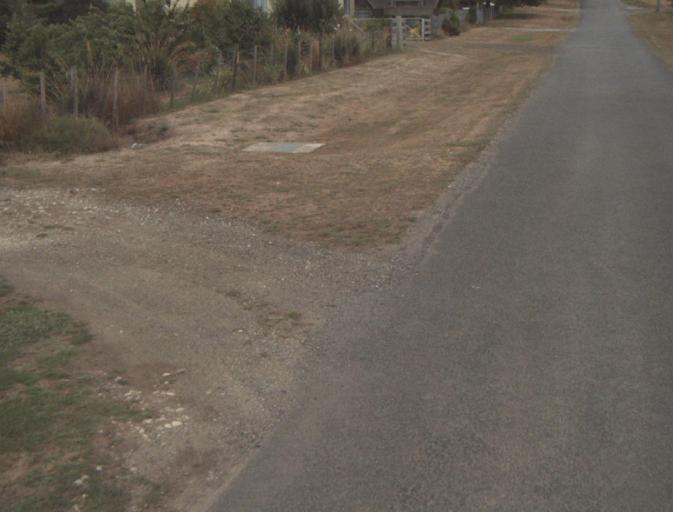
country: AU
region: Tasmania
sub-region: Launceston
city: Mayfield
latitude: -41.2492
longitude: 147.2097
